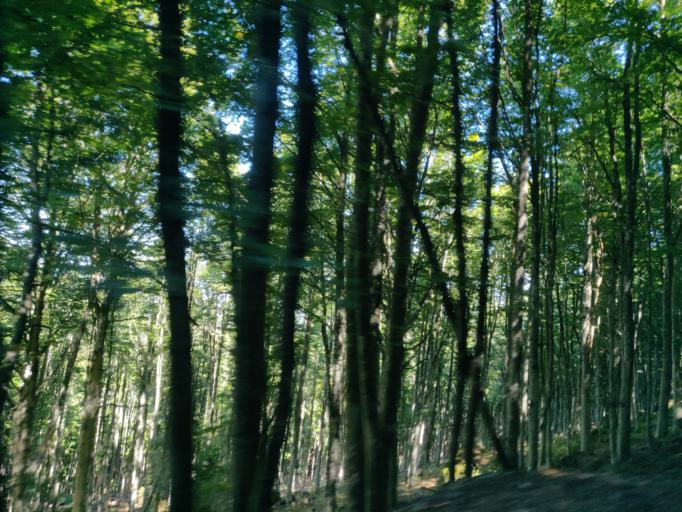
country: IT
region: Tuscany
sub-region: Provincia di Siena
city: Abbadia San Salvatore
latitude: 42.8949
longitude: 11.6310
